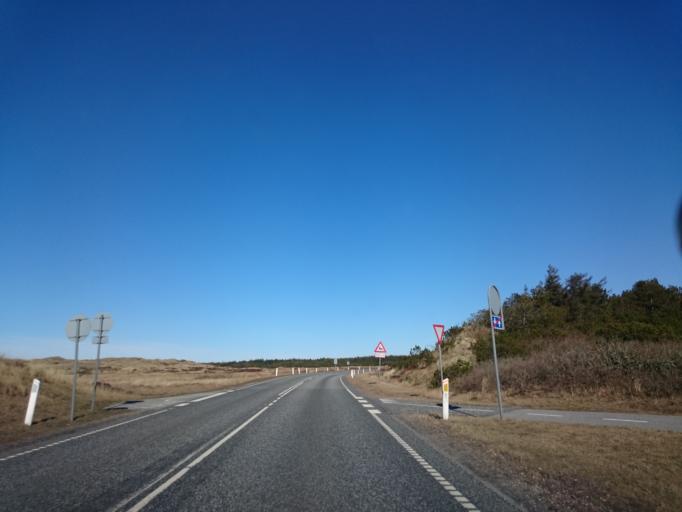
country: DK
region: North Denmark
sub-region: Frederikshavn Kommune
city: Skagen
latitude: 57.6954
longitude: 10.4762
